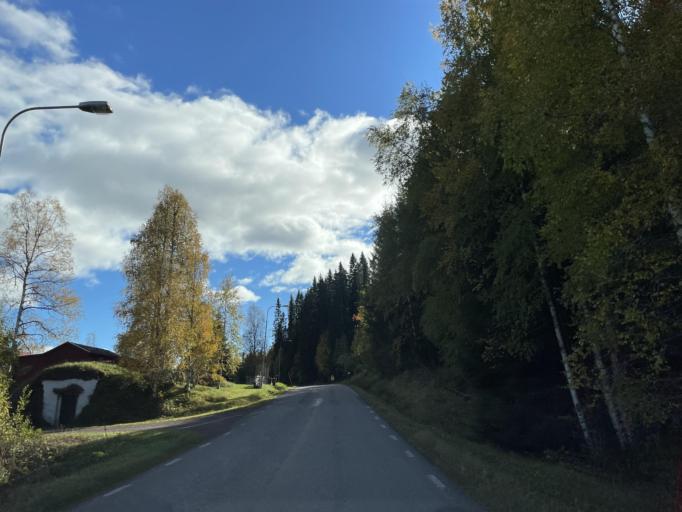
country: SE
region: Dalarna
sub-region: Malung-Saelens kommun
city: Malung
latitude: 61.1543
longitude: 13.2580
